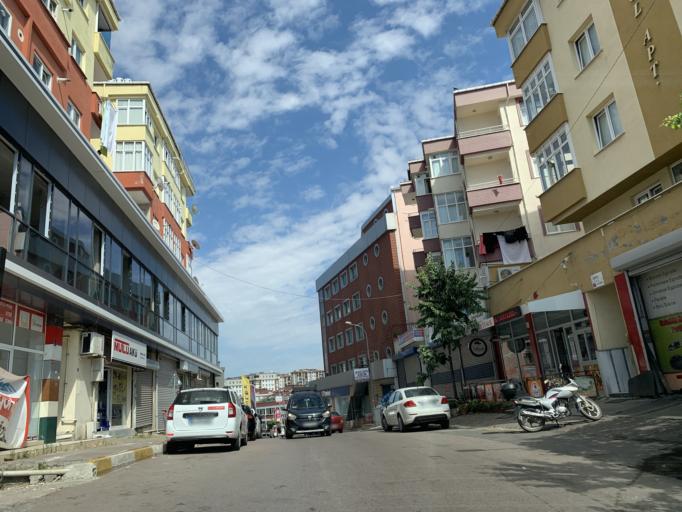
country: TR
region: Istanbul
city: Pendik
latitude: 40.8952
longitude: 29.2465
